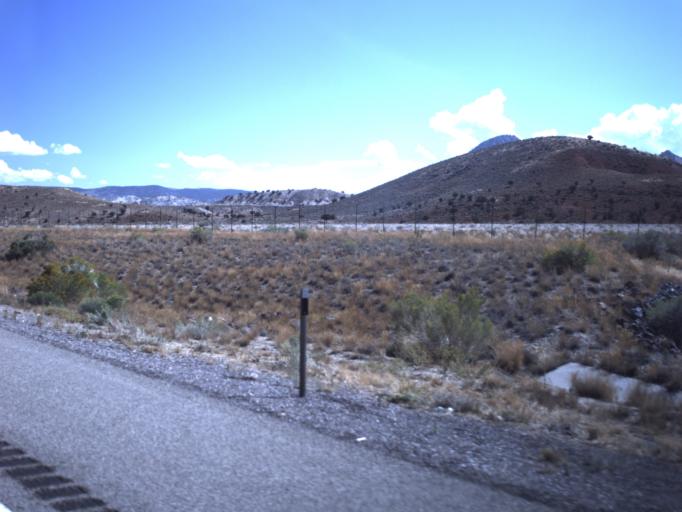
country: US
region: Utah
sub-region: Sevier County
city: Aurora
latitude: 38.8840
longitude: -111.9200
